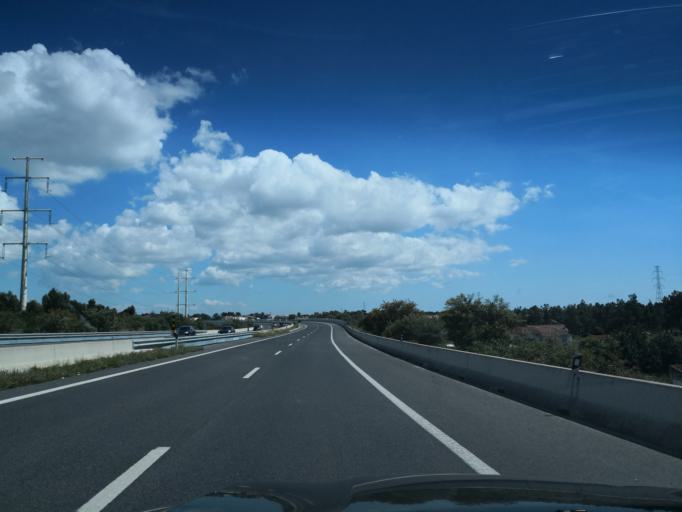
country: PT
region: Setubal
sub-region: Almada
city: Charneca
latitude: 38.6135
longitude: -9.1689
